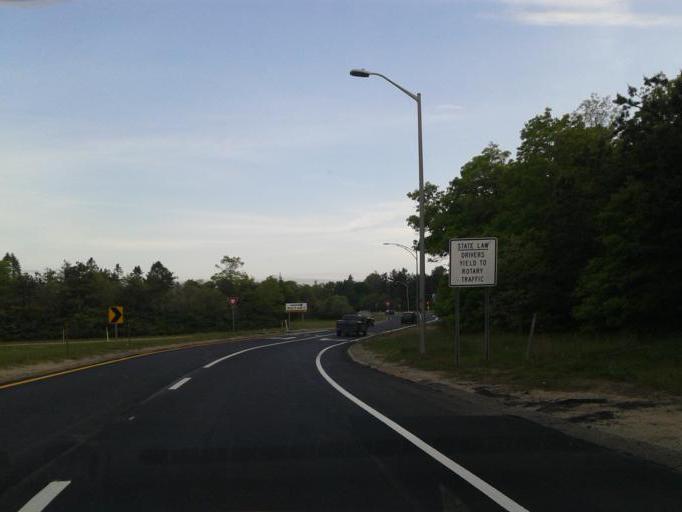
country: US
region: Massachusetts
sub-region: Barnstable County
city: Pocasset
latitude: 41.6870
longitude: -70.5913
